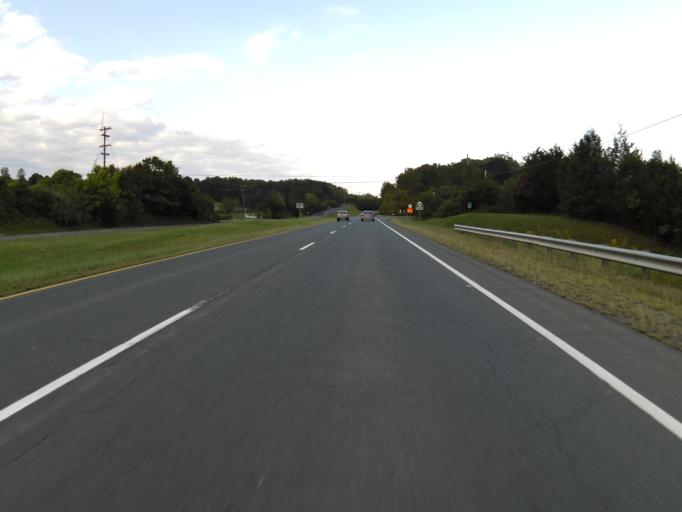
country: US
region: Virginia
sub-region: Fauquier County
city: Warrenton
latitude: 38.6911
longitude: -77.8958
